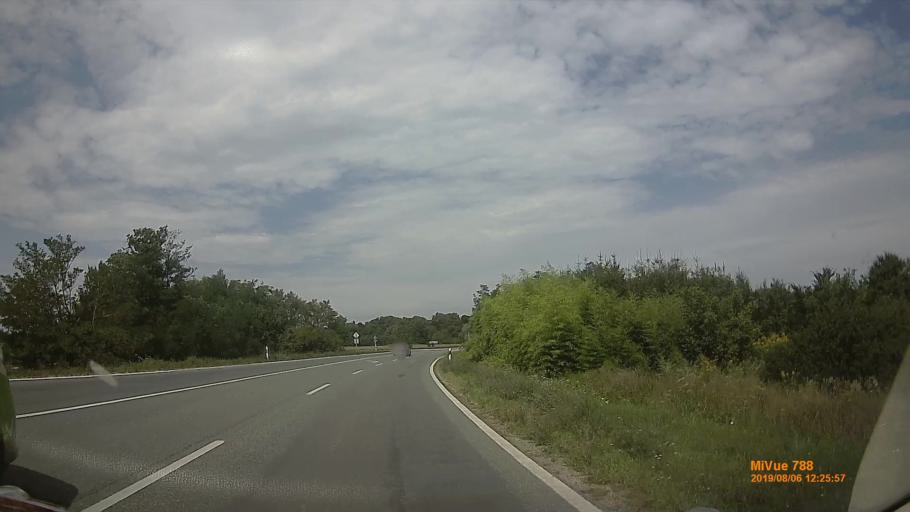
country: HU
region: Vas
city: Taplanszentkereszt
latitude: 47.1991
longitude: 16.6805
